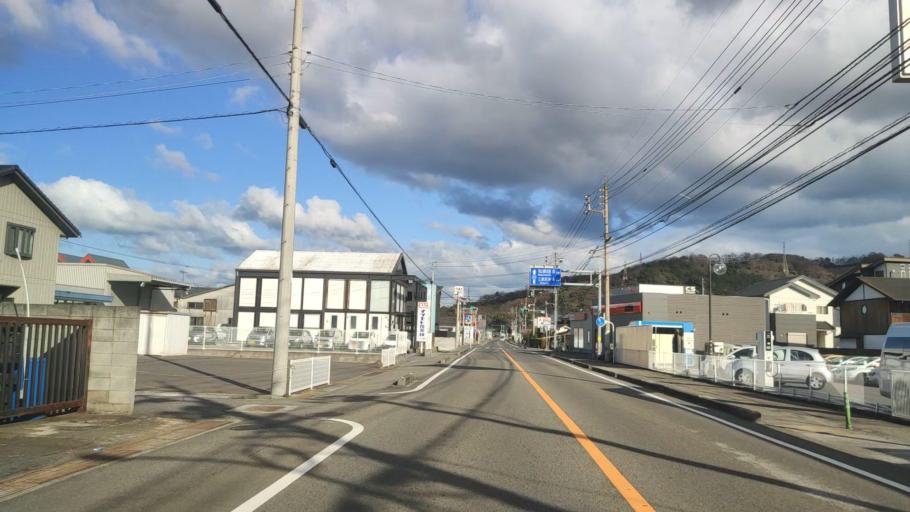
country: JP
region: Ehime
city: Masaki-cho
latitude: 33.8345
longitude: 132.7092
